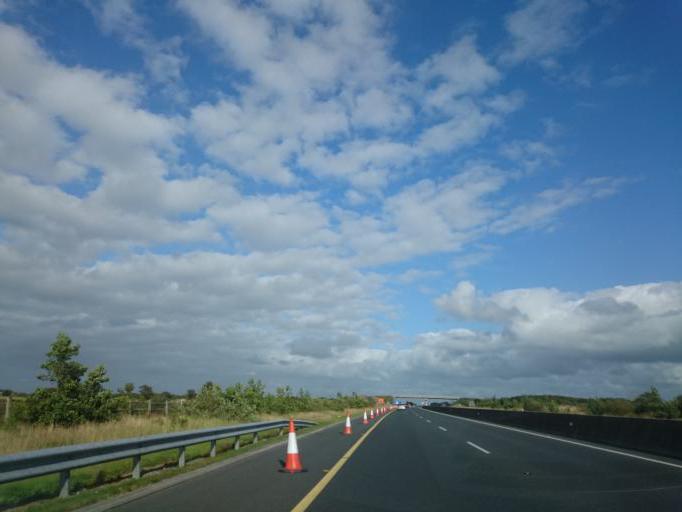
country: IE
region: Connaught
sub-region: County Galway
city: Athenry
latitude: 53.2972
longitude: -8.8011
